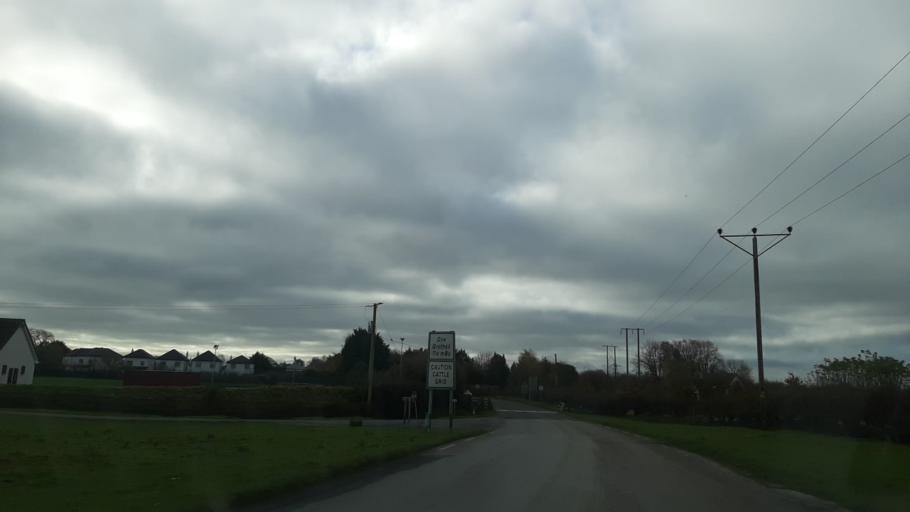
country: IE
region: Leinster
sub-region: Kildare
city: Kildare
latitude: 53.1729
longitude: -6.8996
